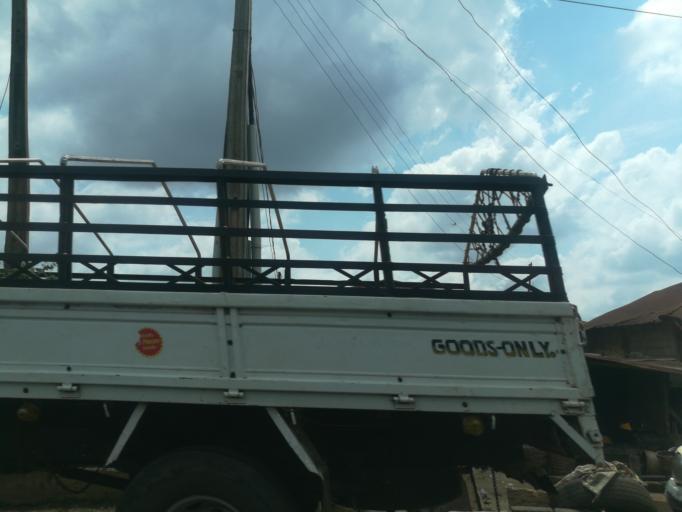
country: NG
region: Oyo
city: Ibadan
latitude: 7.3863
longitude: 3.9052
